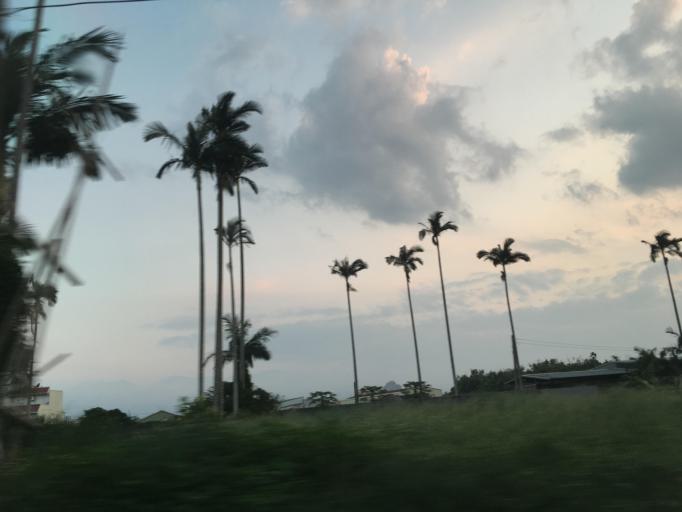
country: TW
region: Taiwan
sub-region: Yilan
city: Yilan
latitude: 24.6906
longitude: 121.7857
